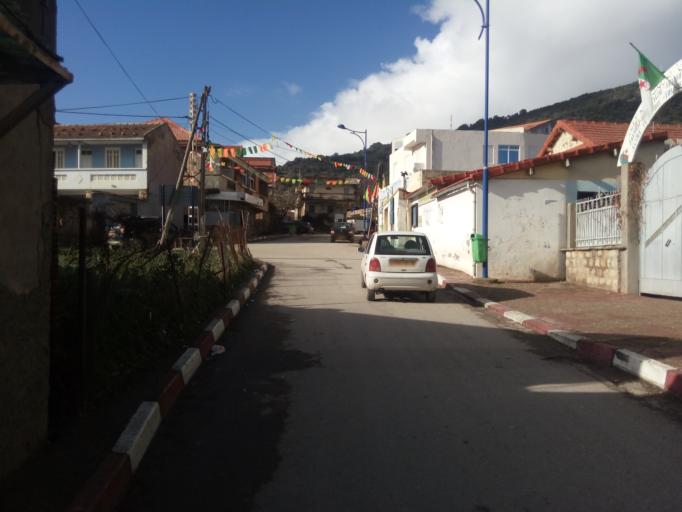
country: DZ
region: Tizi Ouzou
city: Chemini
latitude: 36.6134
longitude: 4.6511
